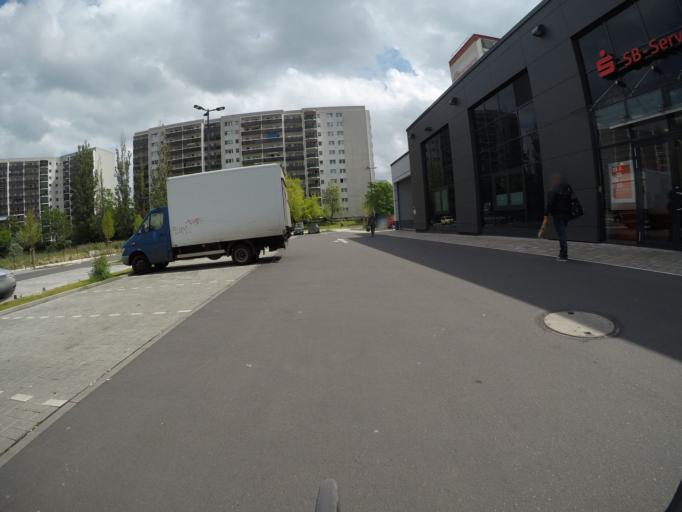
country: DE
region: Berlin
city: Marzahn
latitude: 52.5414
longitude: 13.5653
